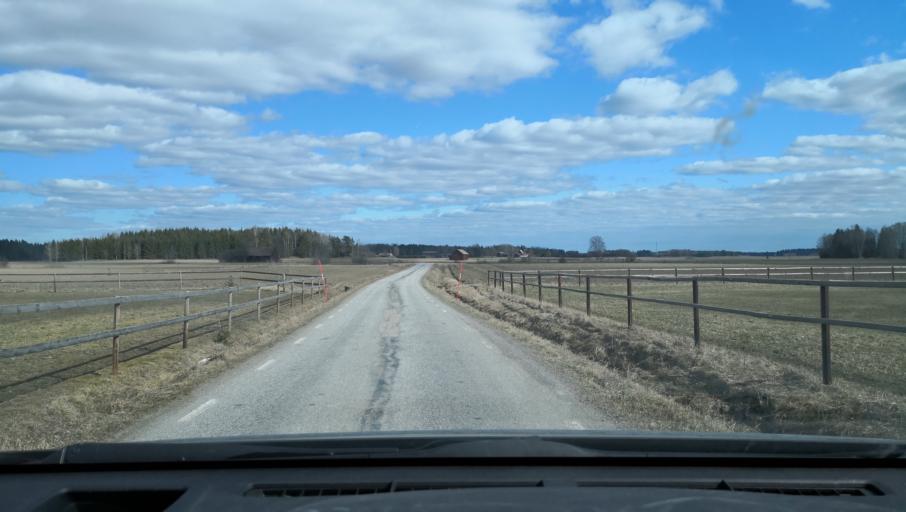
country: SE
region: Vaestmanland
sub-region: Sala Kommun
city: Sala
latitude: 59.8617
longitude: 16.5772
